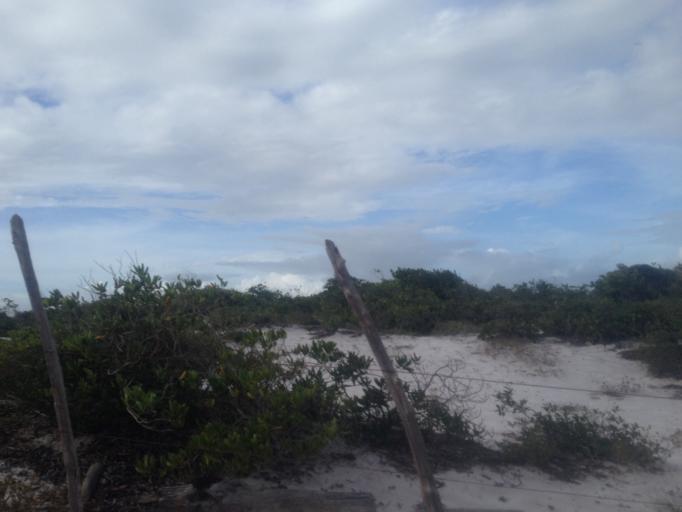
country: BR
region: Bahia
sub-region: Mata De Sao Joao
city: Mata de Sao Joao
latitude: -12.4511
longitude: -37.9344
